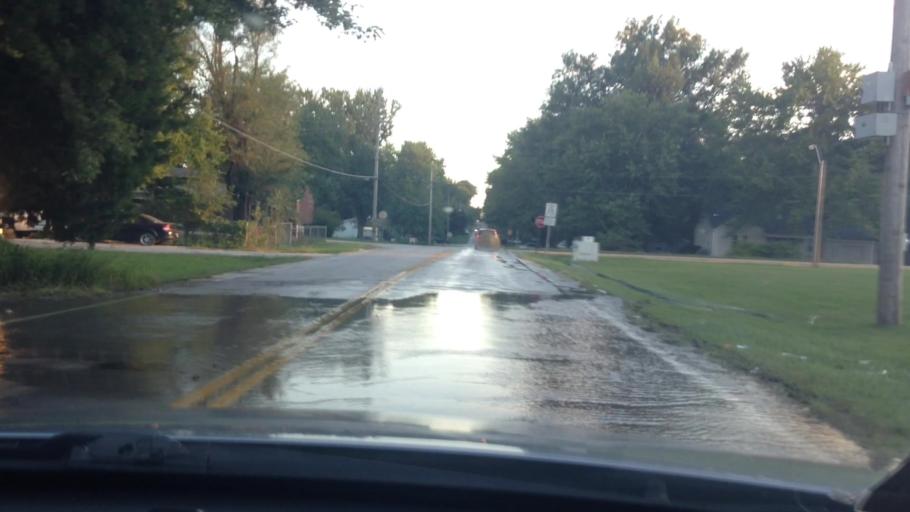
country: US
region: Missouri
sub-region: Jackson County
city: Raytown
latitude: 38.9743
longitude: -94.4930
